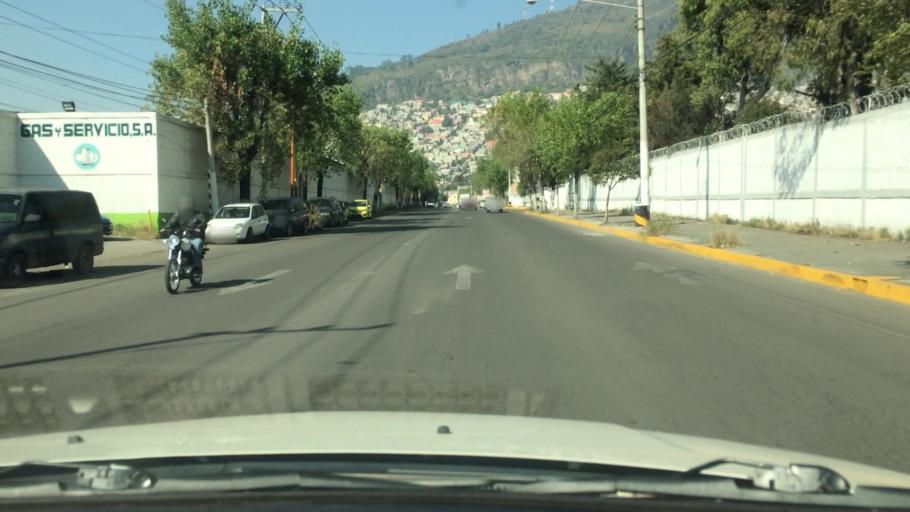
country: MX
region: Mexico
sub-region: Tlalnepantla de Baz
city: Puerto Escondido (Tepeolulco Puerto Escondido)
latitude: 19.5267
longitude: -99.1144
